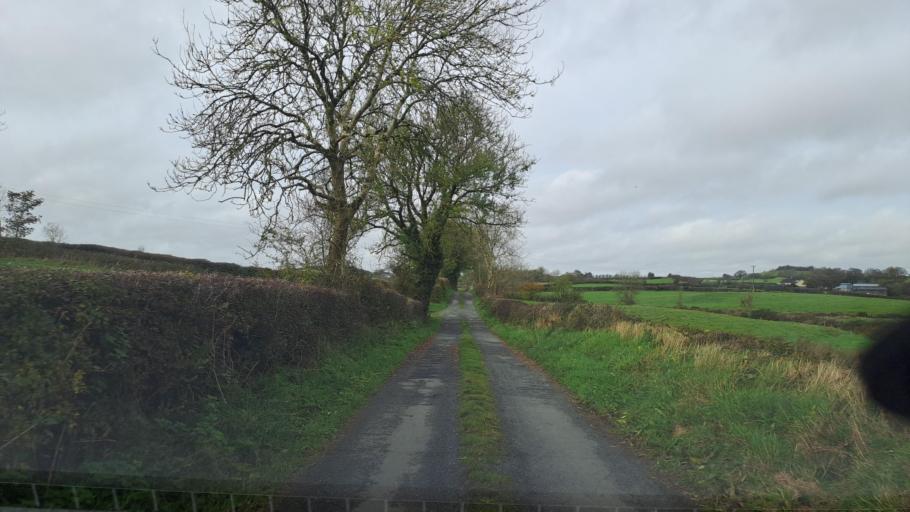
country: IE
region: Ulster
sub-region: County Monaghan
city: Carrickmacross
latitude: 54.0097
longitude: -6.7951
